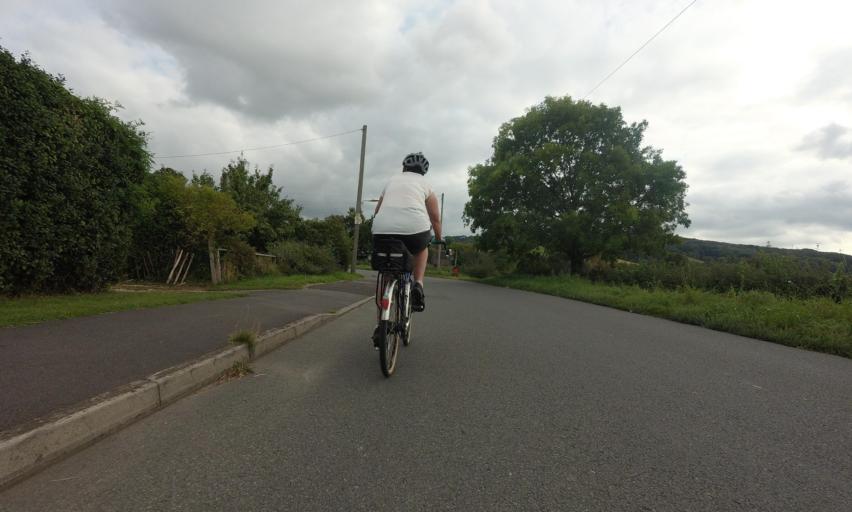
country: GB
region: England
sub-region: Gloucestershire
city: Winchcombe
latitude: 51.9739
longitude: -1.9947
